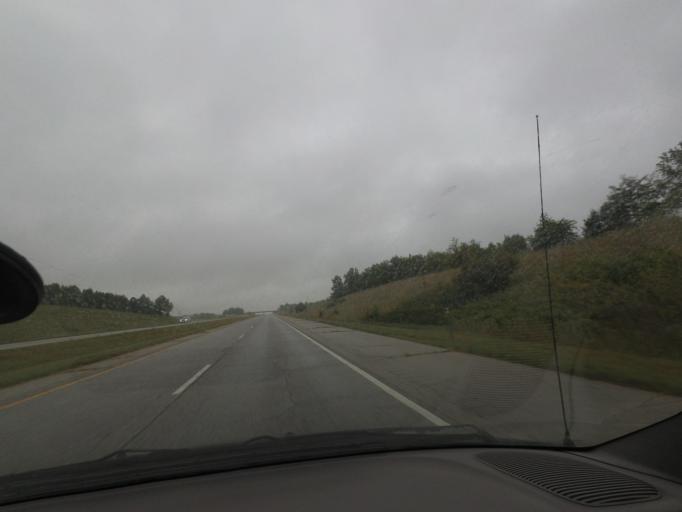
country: US
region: Illinois
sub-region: Pike County
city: Barry
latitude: 39.7069
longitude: -91.0484
